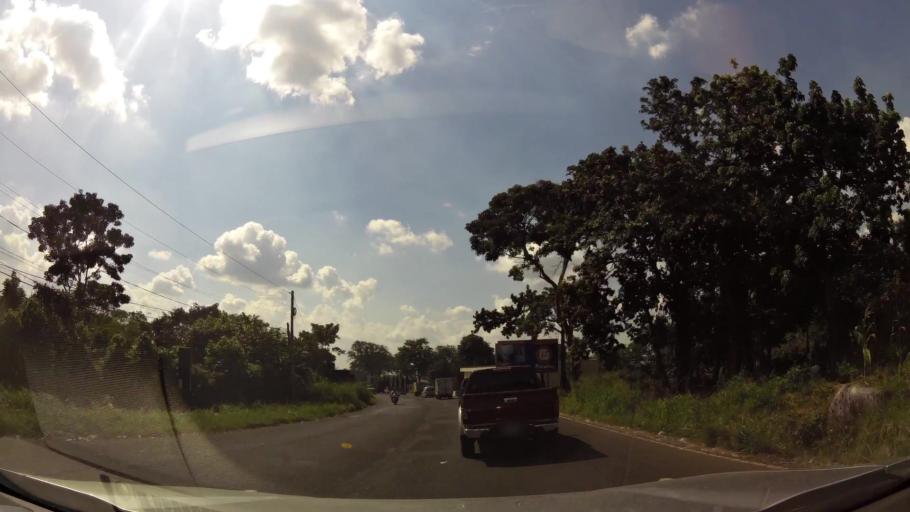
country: GT
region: Suchitepeque
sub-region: Municipio de Cuyotenango
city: Cuyotenango
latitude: 14.5447
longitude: -91.5661
